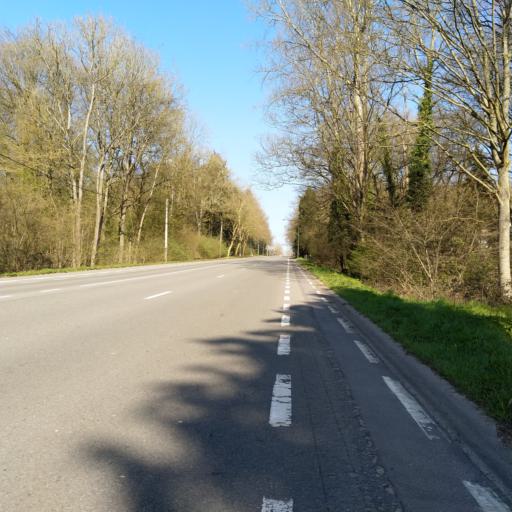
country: BE
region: Wallonia
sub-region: Province du Hainaut
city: Jurbise
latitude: 50.4962
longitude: 3.9371
